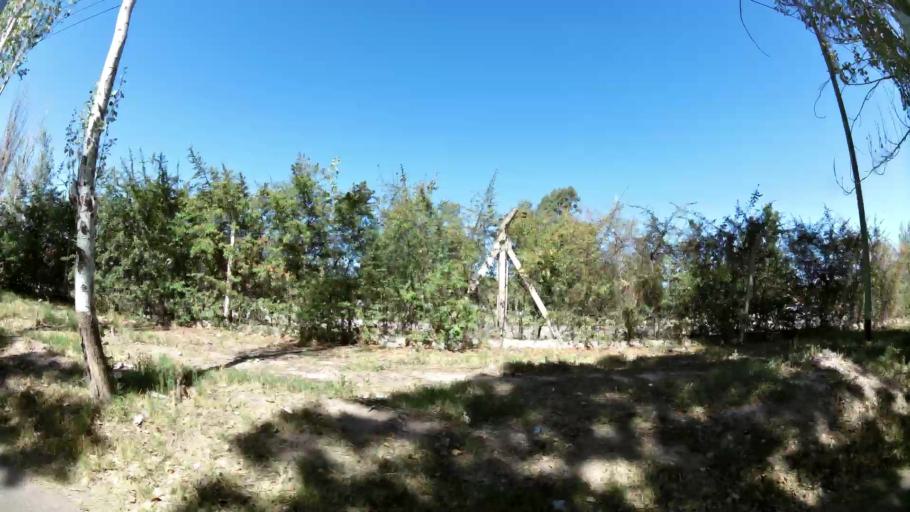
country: AR
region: Mendoza
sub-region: Departamento de Godoy Cruz
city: Godoy Cruz
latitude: -32.9762
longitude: -68.8402
